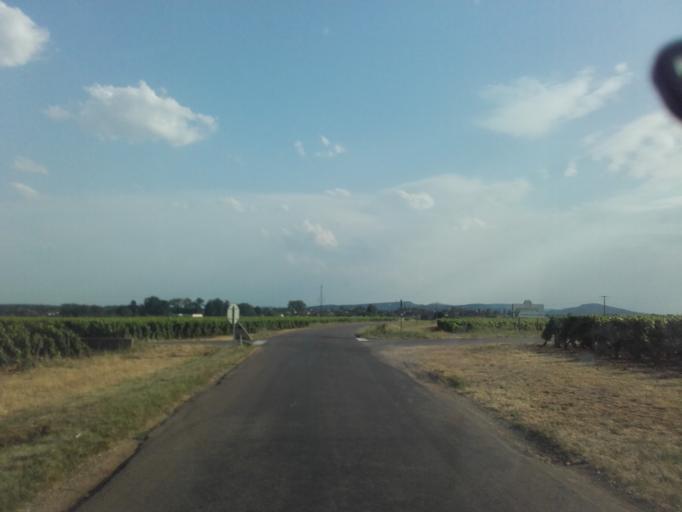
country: FR
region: Bourgogne
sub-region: Departement de la Cote-d'Or
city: Meursault
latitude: 46.9566
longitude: 4.7574
